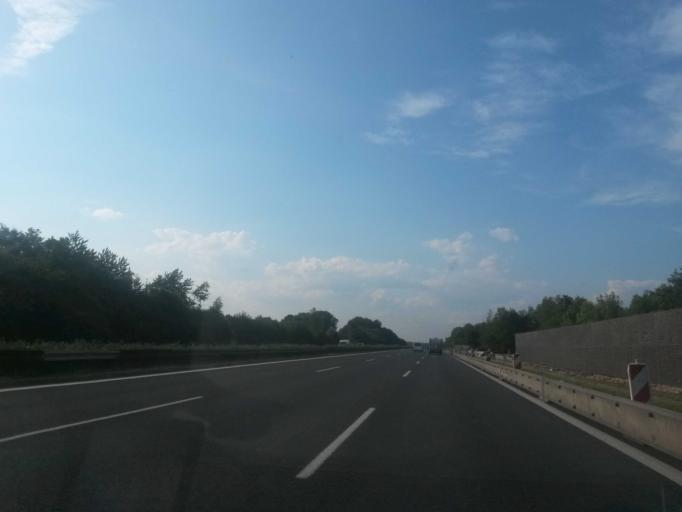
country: DE
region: Bavaria
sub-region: Regierungsbezirk Mittelfranken
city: Allersberg
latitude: 49.2220
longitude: 11.2250
